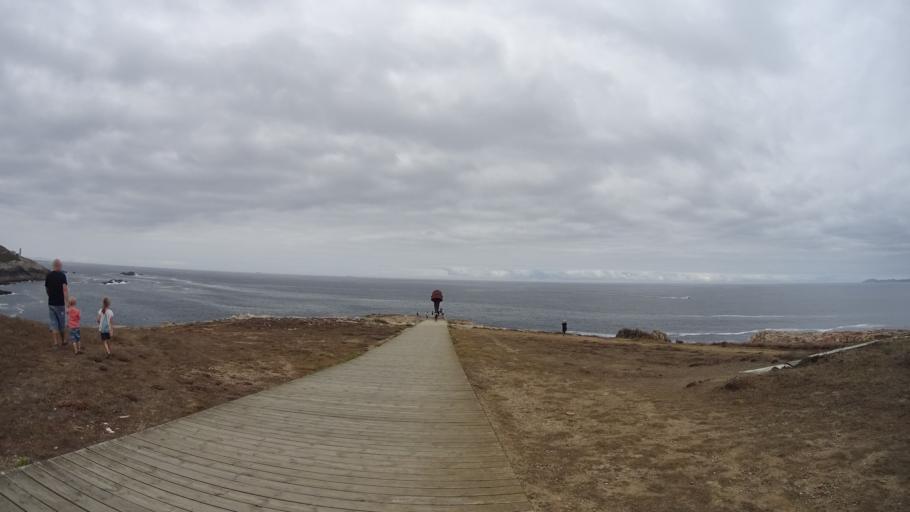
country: ES
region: Galicia
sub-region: Provincia da Coruna
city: A Coruna
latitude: 43.3885
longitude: -8.4001
